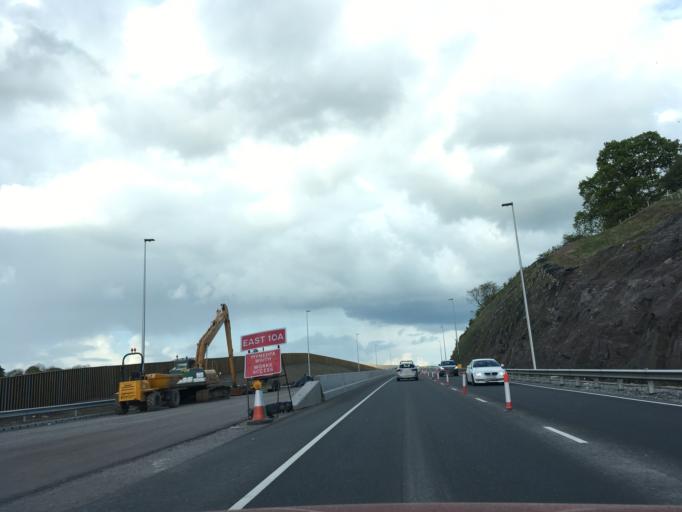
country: GB
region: Wales
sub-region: Monmouthshire
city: Gilwern
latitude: 51.8182
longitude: -3.1104
